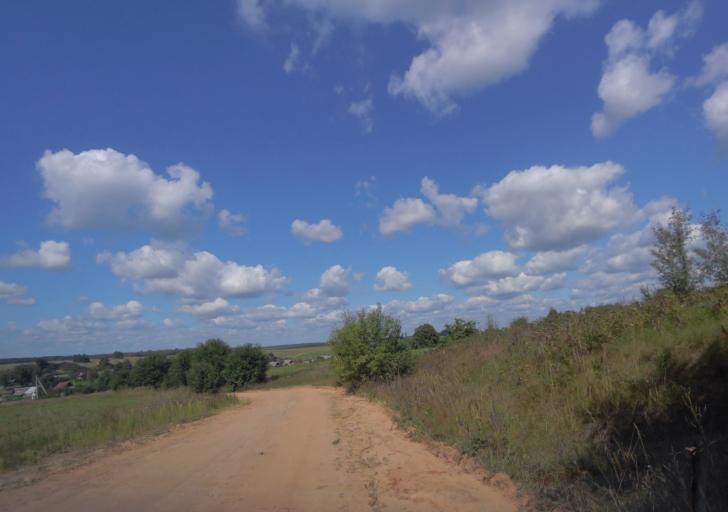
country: BY
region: Minsk
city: Horad Barysaw
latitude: 54.3704
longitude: 28.4549
